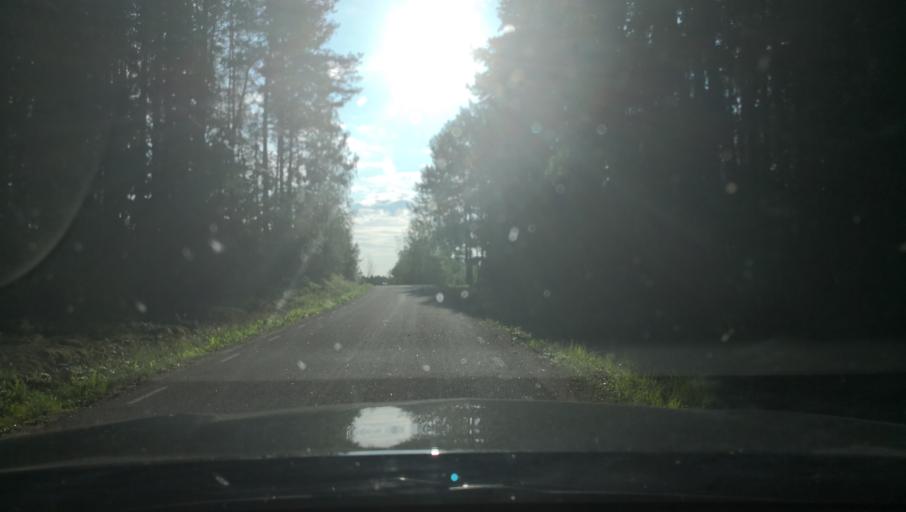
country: SE
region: Uppsala
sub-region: Osthammars Kommun
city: Osterbybruk
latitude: 60.0172
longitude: 17.9284
